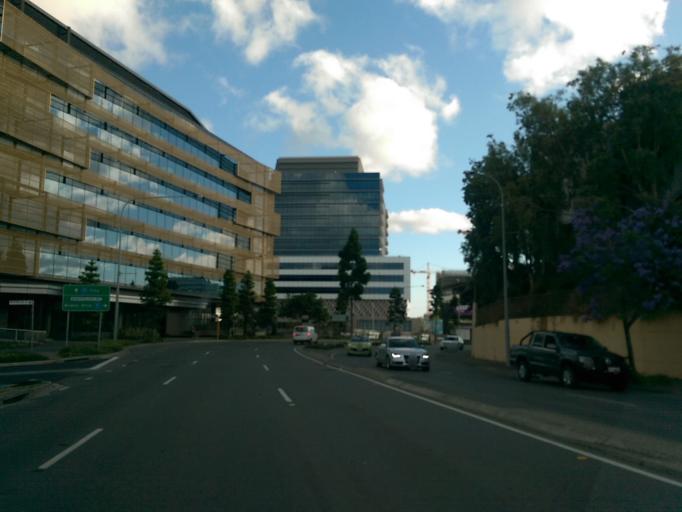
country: AU
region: Queensland
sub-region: Brisbane
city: Fortitude Valley
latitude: -27.4483
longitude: 153.0426
